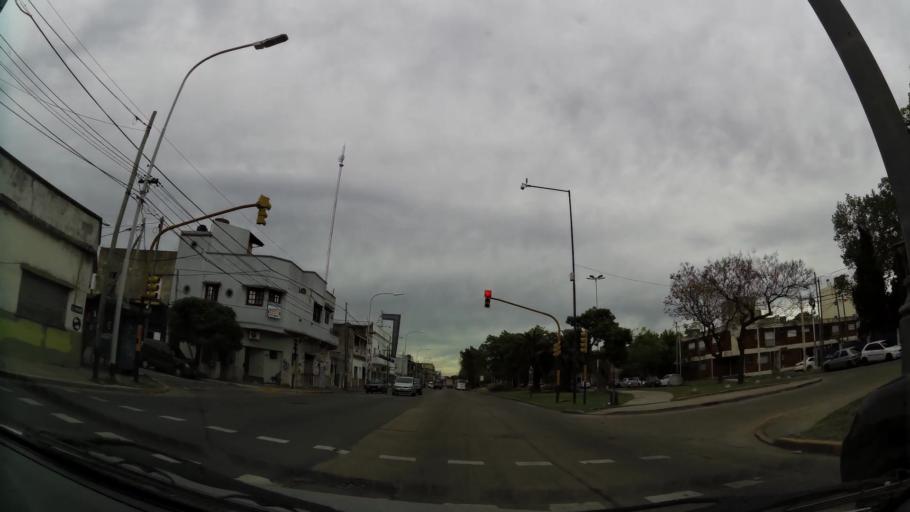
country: AR
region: Buenos Aires
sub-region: Partido de Avellaneda
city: Avellaneda
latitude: -34.6809
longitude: -58.3654
